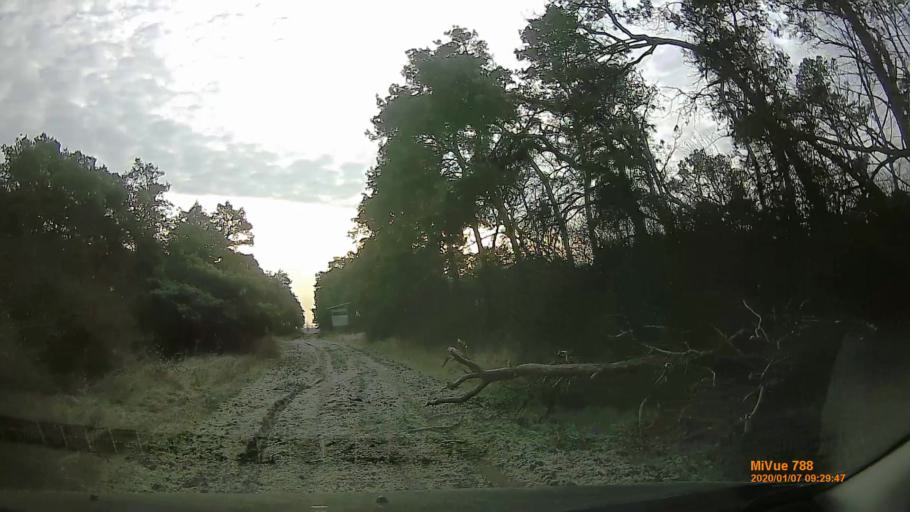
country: HU
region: Gyor-Moson-Sopron
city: Rajka
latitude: 47.9482
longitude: 17.1710
